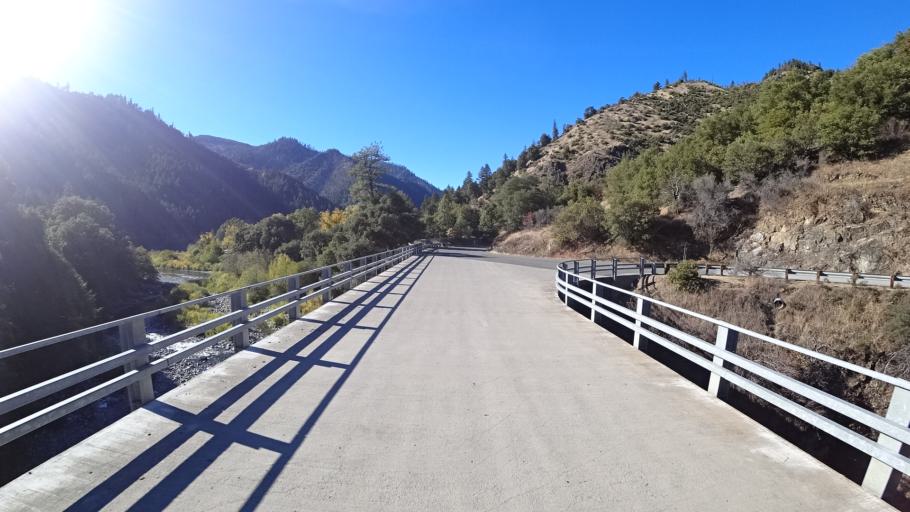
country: US
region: California
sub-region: Humboldt County
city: Willow Creek
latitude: 41.2570
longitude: -123.3212
